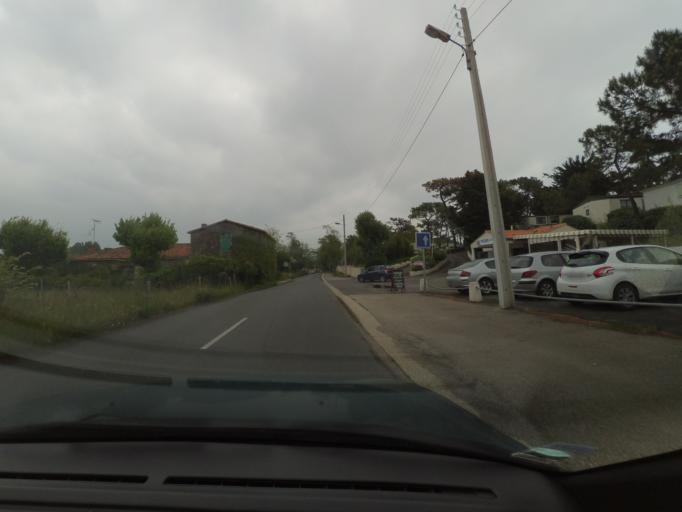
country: FR
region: Pays de la Loire
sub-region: Departement de la Vendee
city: Angles
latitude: 46.3489
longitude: -1.3613
